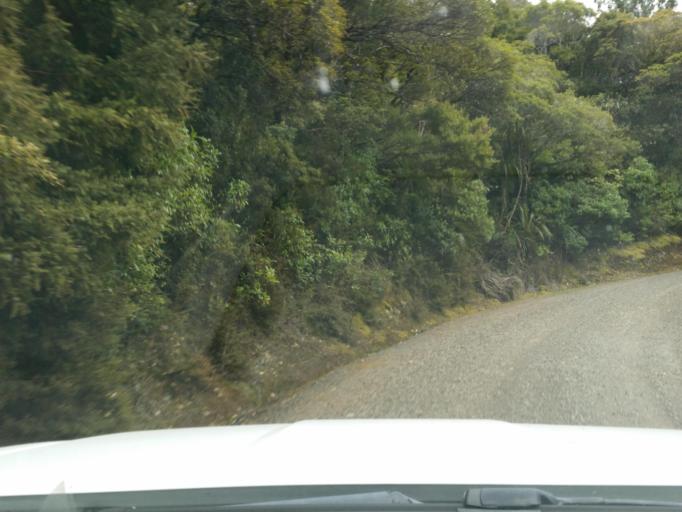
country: NZ
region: Northland
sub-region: Kaipara District
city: Dargaville
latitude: -35.7112
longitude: 173.6313
